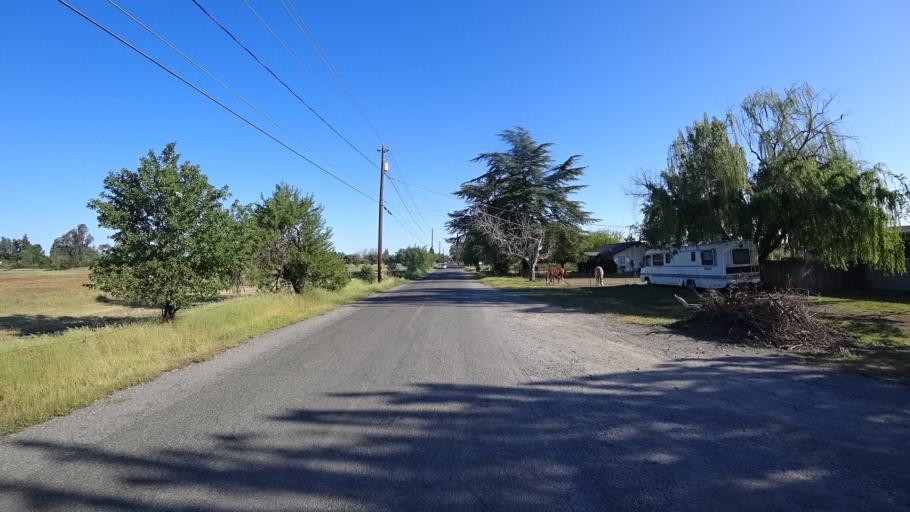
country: US
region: California
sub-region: Glenn County
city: Orland
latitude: 39.7334
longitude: -122.1876
